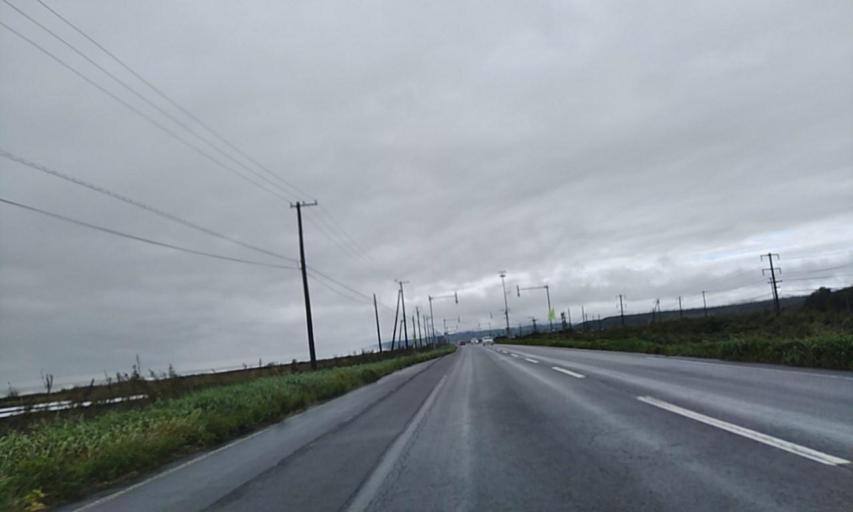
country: JP
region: Hokkaido
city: Kushiro
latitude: 42.9965
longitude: 144.2138
